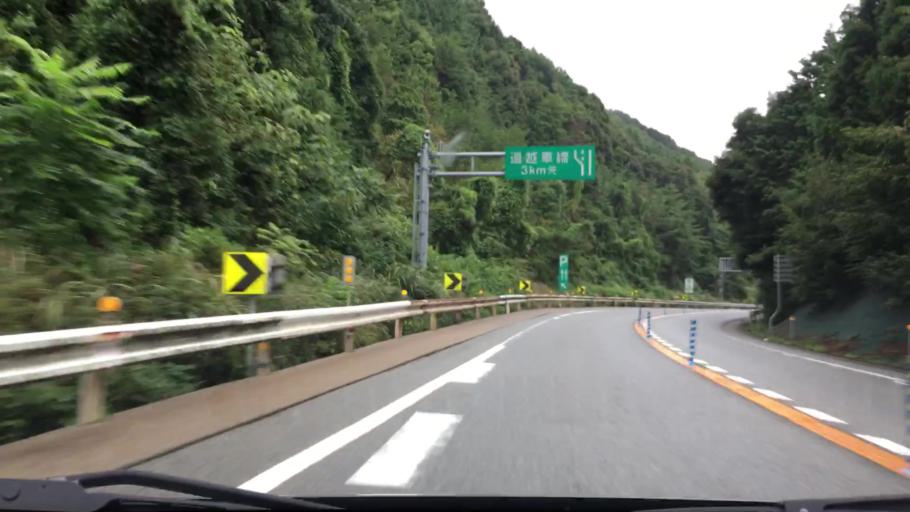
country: JP
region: Hyogo
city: Nishiwaki
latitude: 35.0281
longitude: 134.7667
